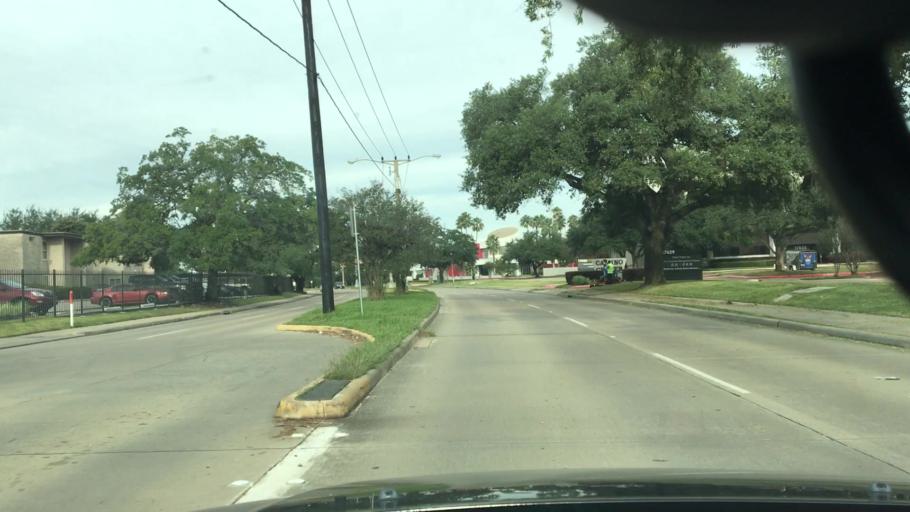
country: US
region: Texas
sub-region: Harris County
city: Webster
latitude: 29.5485
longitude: -95.1086
